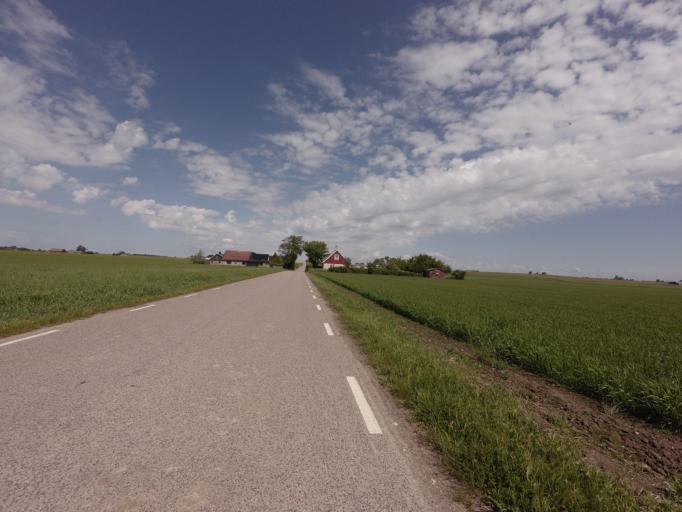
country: SE
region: Skane
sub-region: Trelleborgs Kommun
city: Skare
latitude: 55.4112
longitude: 13.0998
